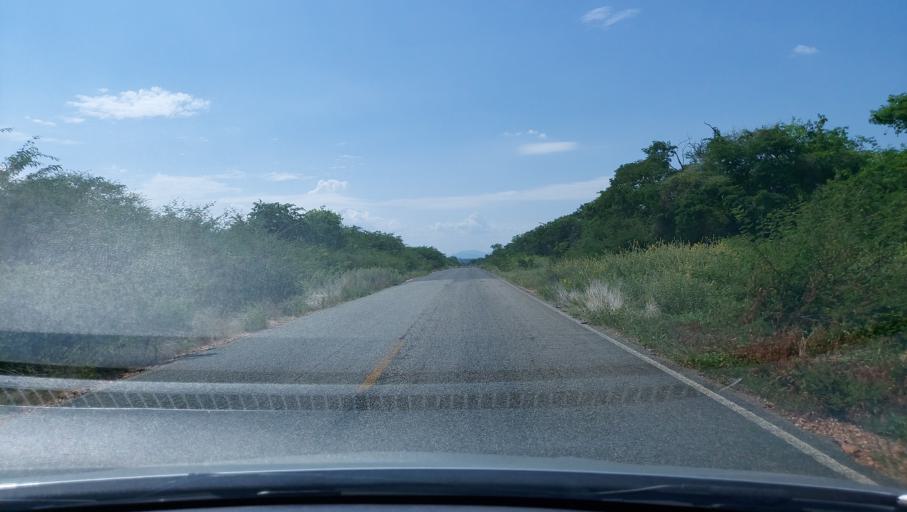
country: BR
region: Bahia
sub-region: Oliveira Dos Brejinhos
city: Beira Rio
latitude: -12.1798
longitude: -42.5423
